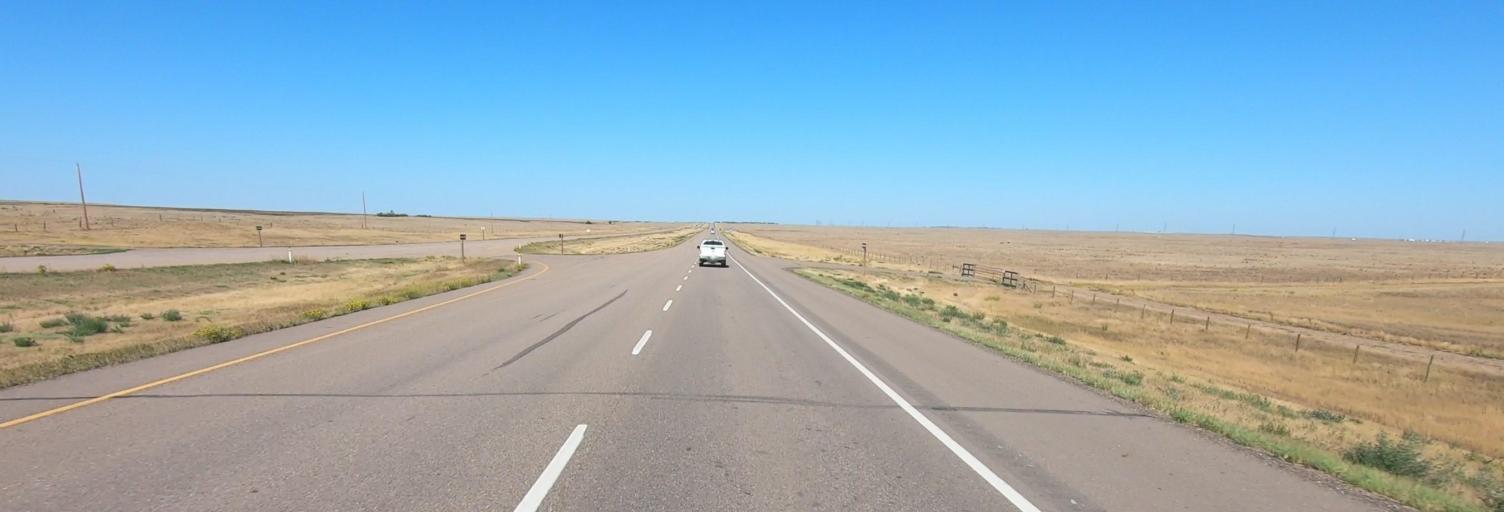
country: CA
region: Alberta
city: Medicine Hat
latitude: 50.1913
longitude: -111.0710
